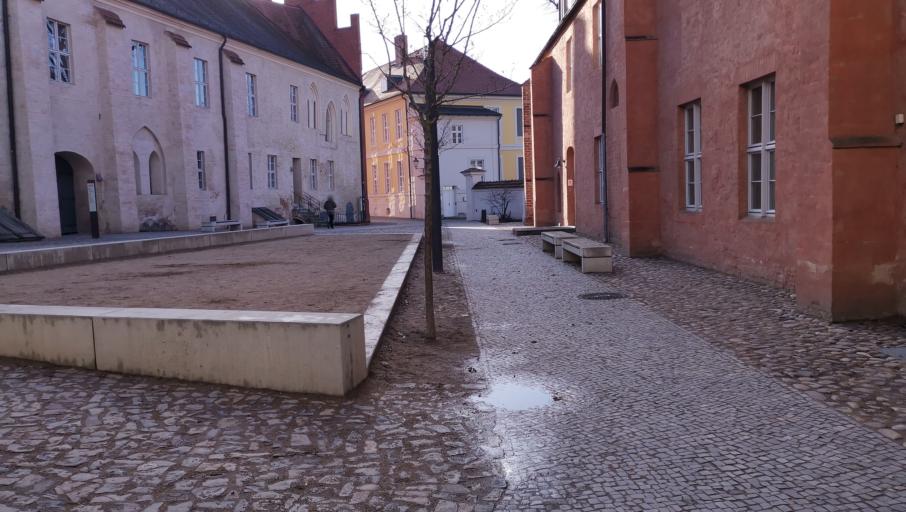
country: DE
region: Brandenburg
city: Brandenburg an der Havel
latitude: 52.4160
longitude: 12.5676
